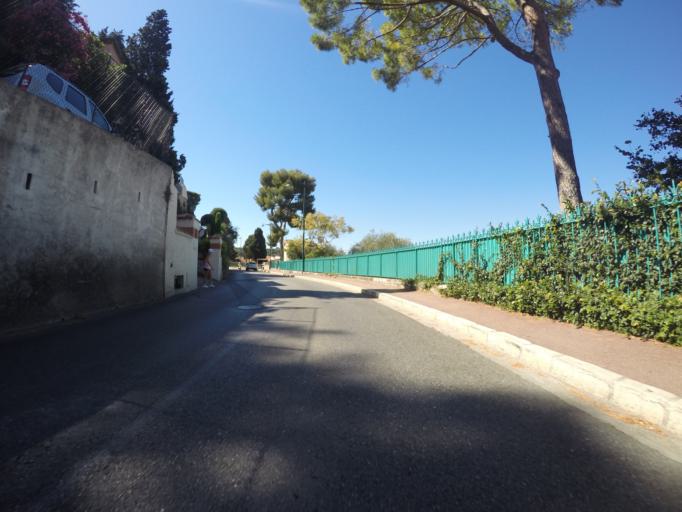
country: FR
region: Provence-Alpes-Cote d'Azur
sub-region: Departement des Alpes-Maritimes
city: Beaulieu-sur-Mer
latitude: 43.6990
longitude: 7.3261
